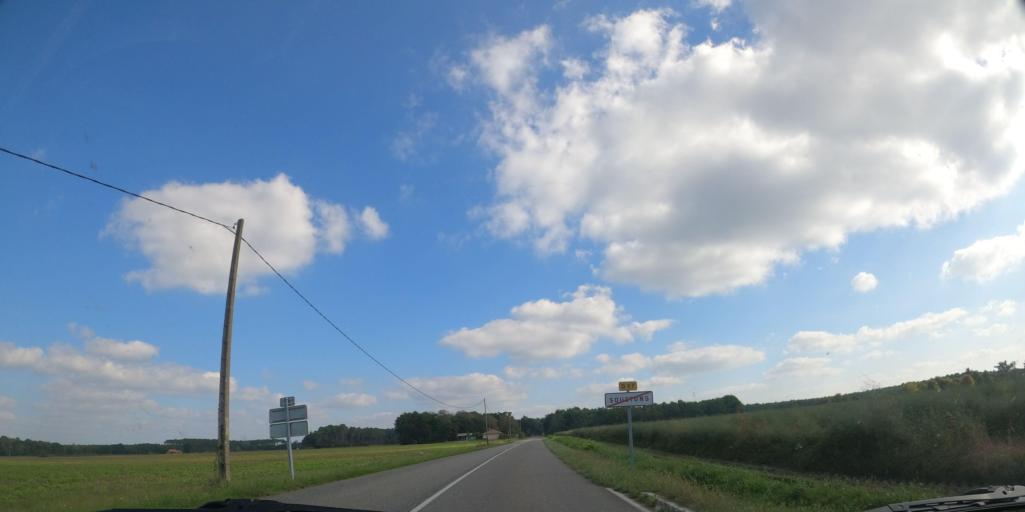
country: FR
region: Aquitaine
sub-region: Departement des Landes
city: Soustons
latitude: 43.7448
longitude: -1.3044
